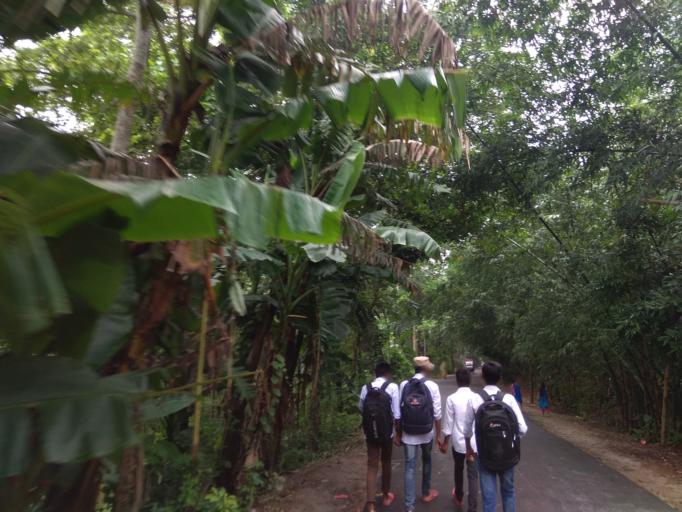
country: BD
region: Dhaka
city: Dohar
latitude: 23.4711
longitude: 90.0738
